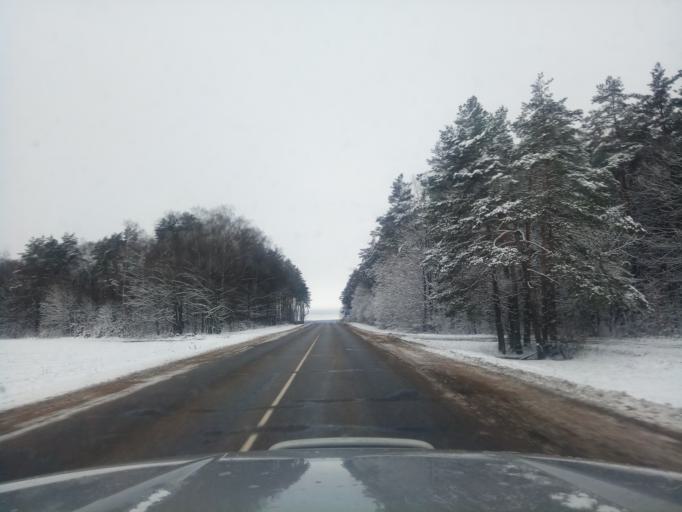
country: BY
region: Minsk
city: Kapyl'
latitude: 53.1561
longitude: 27.1096
